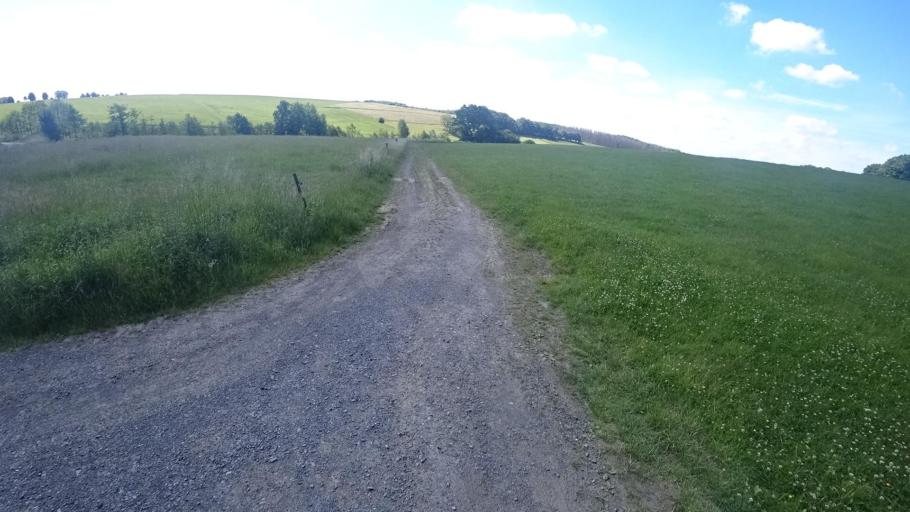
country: DE
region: Rheinland-Pfalz
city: Giesenhausen
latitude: 50.7033
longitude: 7.7055
